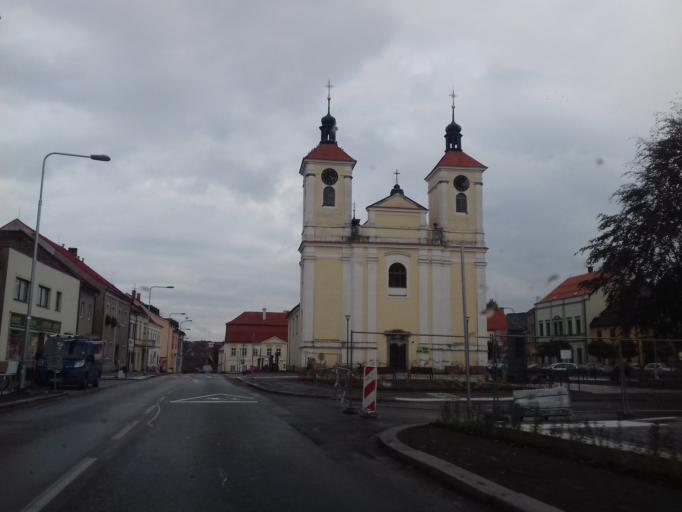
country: CZ
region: Pardubicky
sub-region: Okres Chrudim
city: Chrast
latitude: 49.9017
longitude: 15.9351
